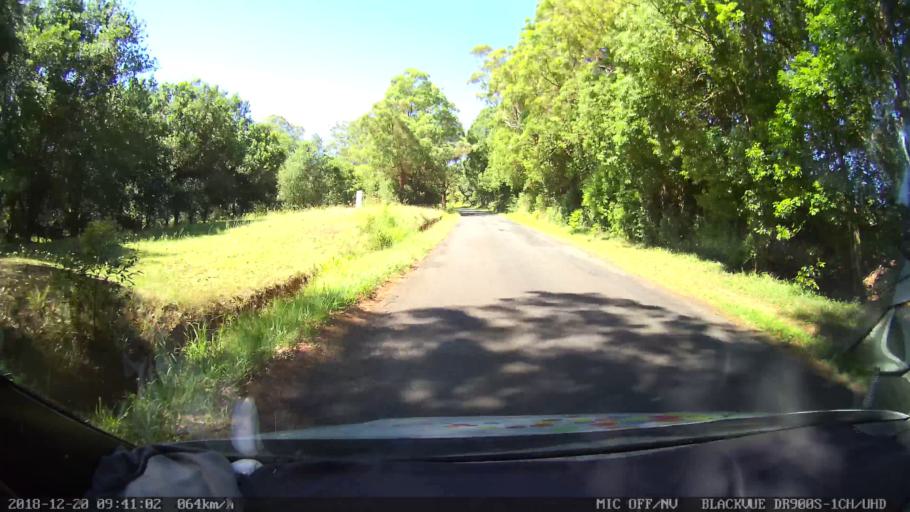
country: AU
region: New South Wales
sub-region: Lismore Municipality
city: Lismore
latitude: -28.7059
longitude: 153.3020
